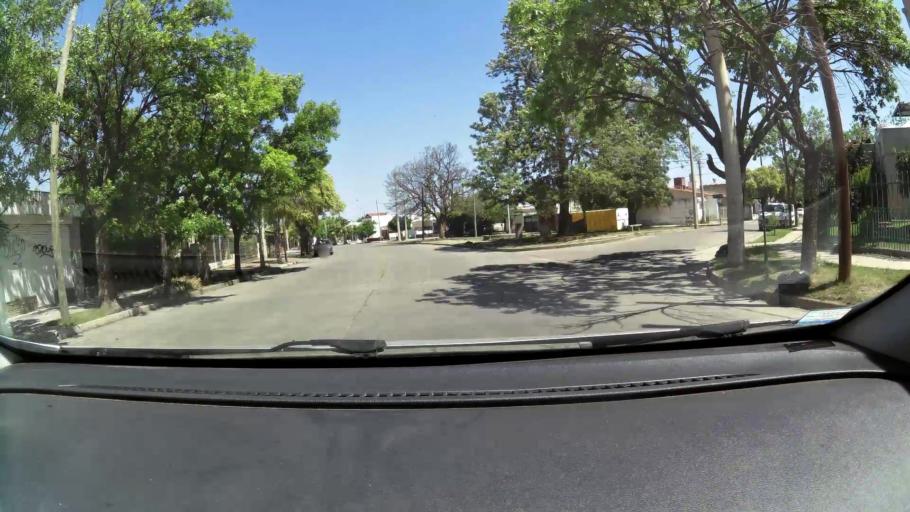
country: AR
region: Cordoba
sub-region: Departamento de Capital
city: Cordoba
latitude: -31.3823
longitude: -64.1656
